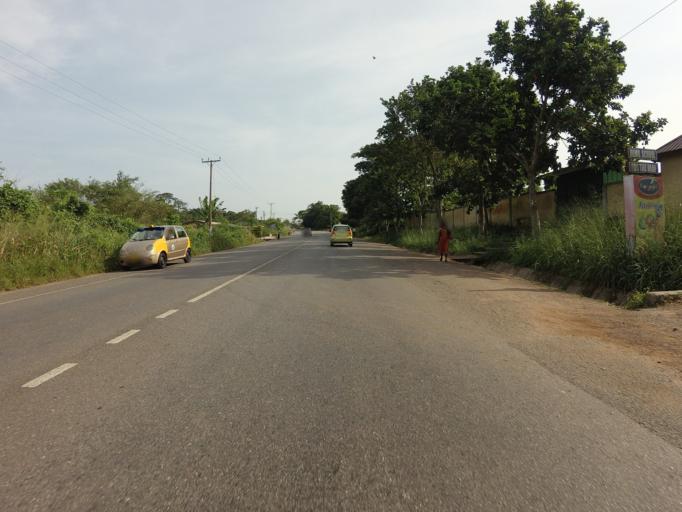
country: GH
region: Eastern
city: Aburi
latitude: 5.9019
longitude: -0.1474
